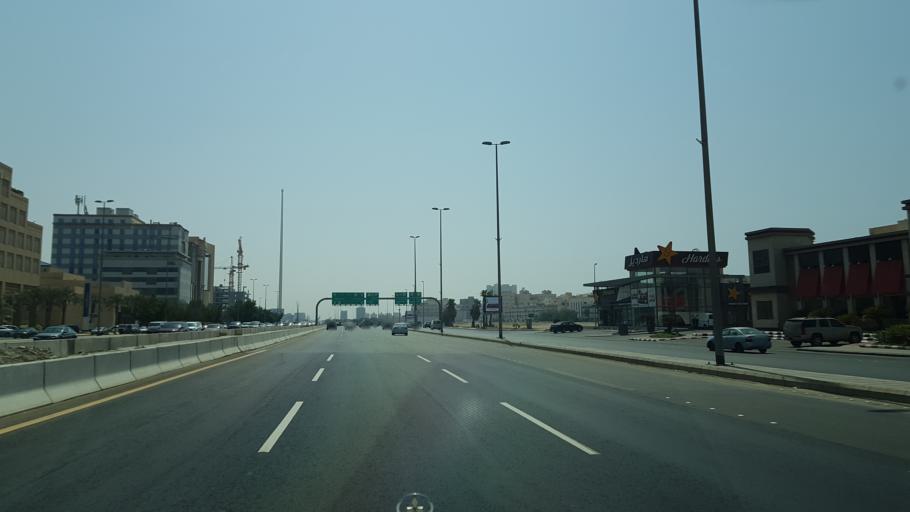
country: SA
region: Makkah
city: Jeddah
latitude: 21.5157
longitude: 39.1664
